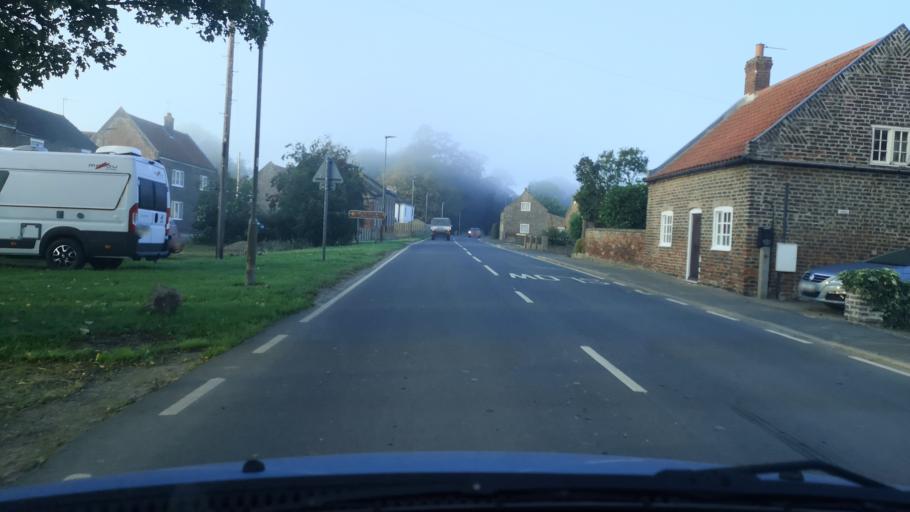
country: GB
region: England
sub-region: North Lincolnshire
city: Eastoft
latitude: 53.6386
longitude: -0.7824
